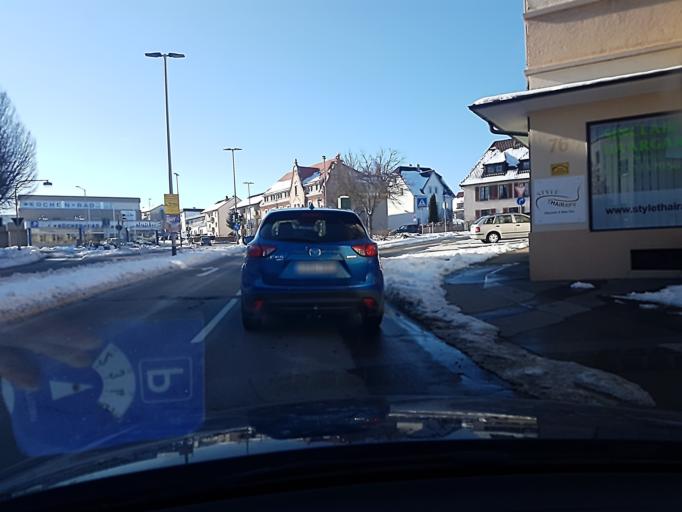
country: DE
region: Baden-Wuerttemberg
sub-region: Freiburg Region
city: Villingen-Schwenningen
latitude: 48.0629
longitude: 8.5230
